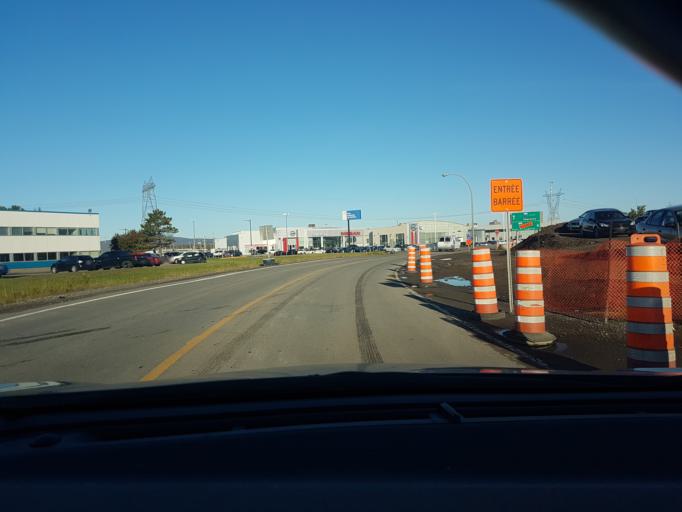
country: CA
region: Quebec
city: L'Ancienne-Lorette
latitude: 46.7937
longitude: -71.3178
